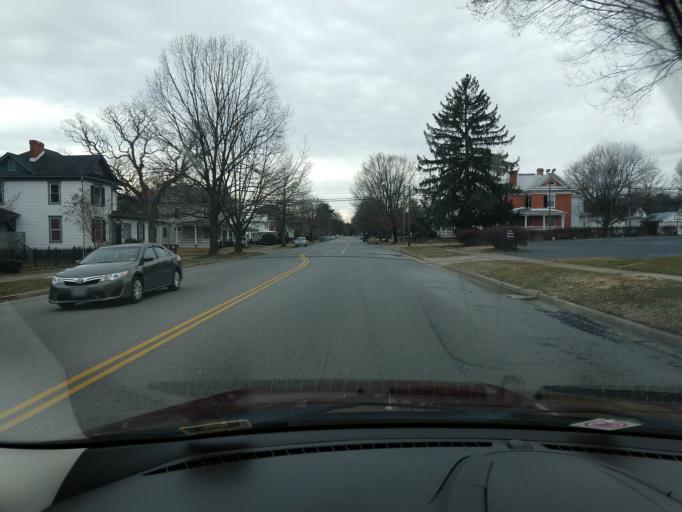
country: US
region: Virginia
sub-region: City of Waynesboro
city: Waynesboro
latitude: 38.0654
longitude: -78.8911
